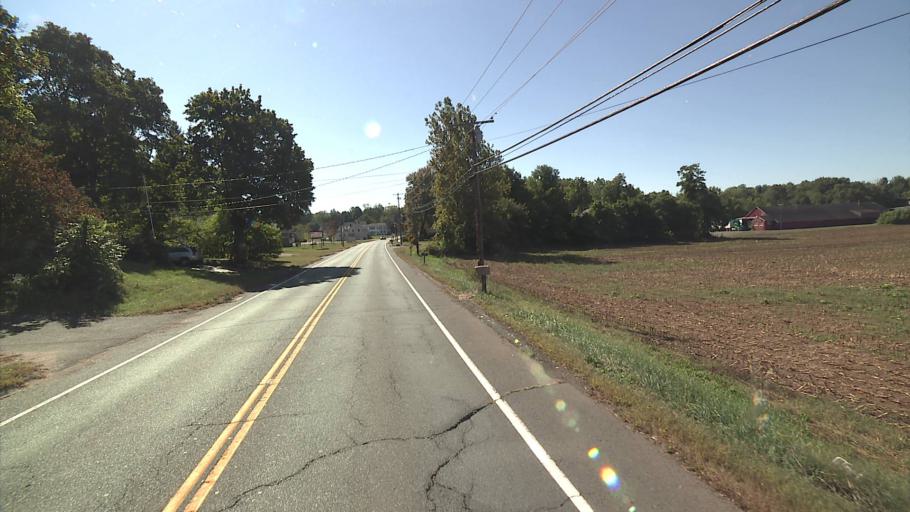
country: US
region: Connecticut
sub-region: Tolland County
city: Rockville
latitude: 41.8750
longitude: -72.4635
